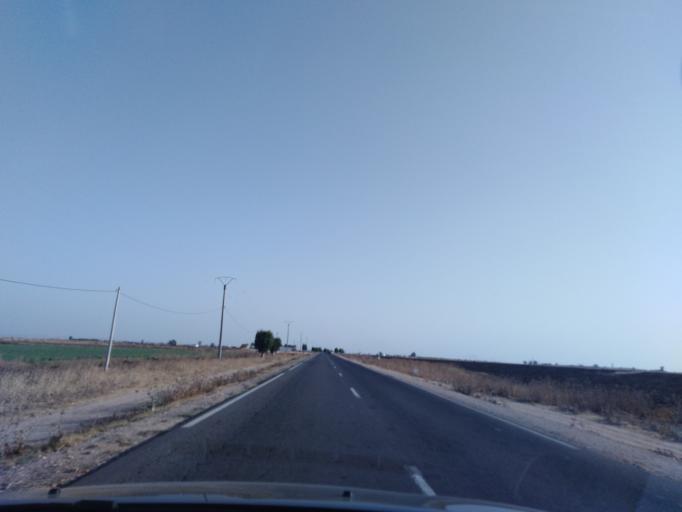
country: MA
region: Doukkala-Abda
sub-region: Safi
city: Youssoufia
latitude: 32.4818
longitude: -8.7687
